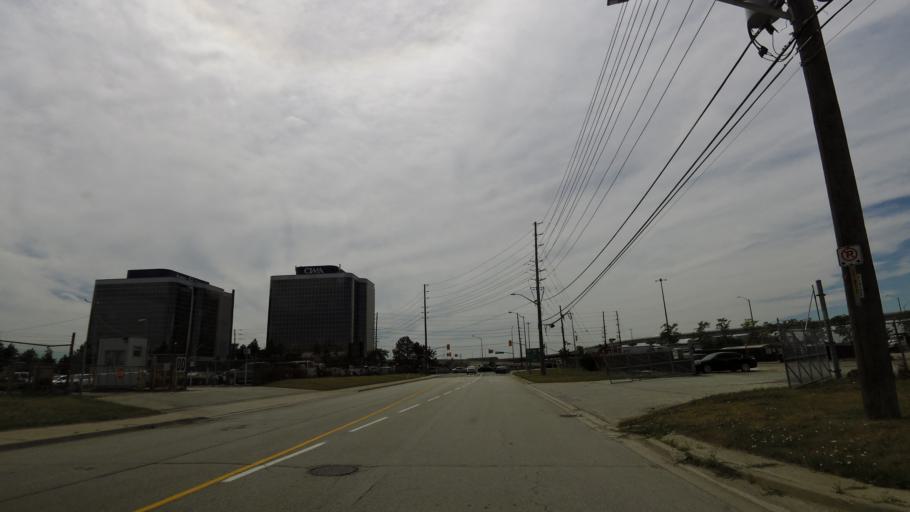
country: CA
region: Ontario
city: Etobicoke
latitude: 43.6897
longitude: -79.6095
